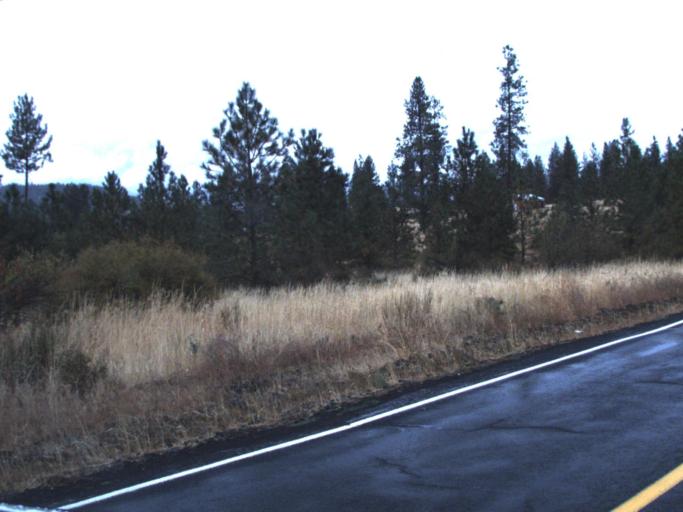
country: US
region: Washington
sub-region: Spokane County
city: Fairchild Air Force Base
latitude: 47.7820
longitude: -117.8887
